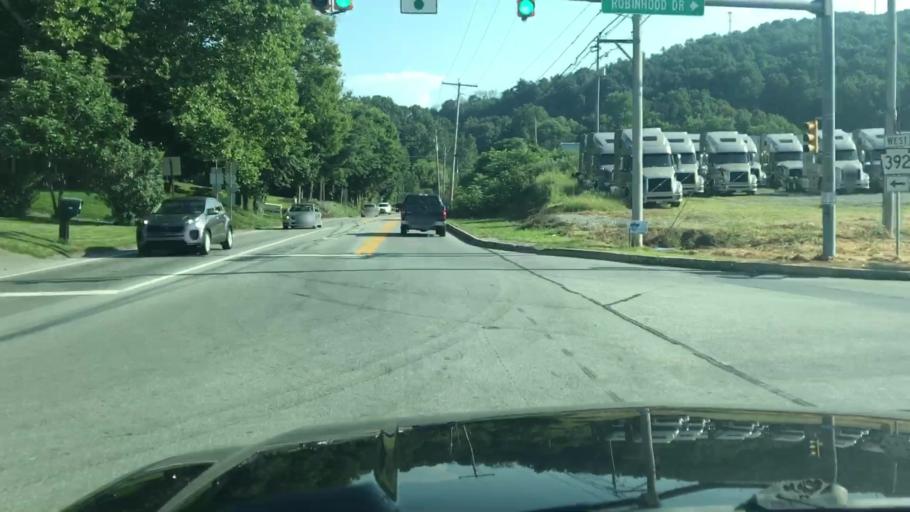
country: US
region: Pennsylvania
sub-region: York County
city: Valley Green
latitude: 40.1531
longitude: -76.8172
